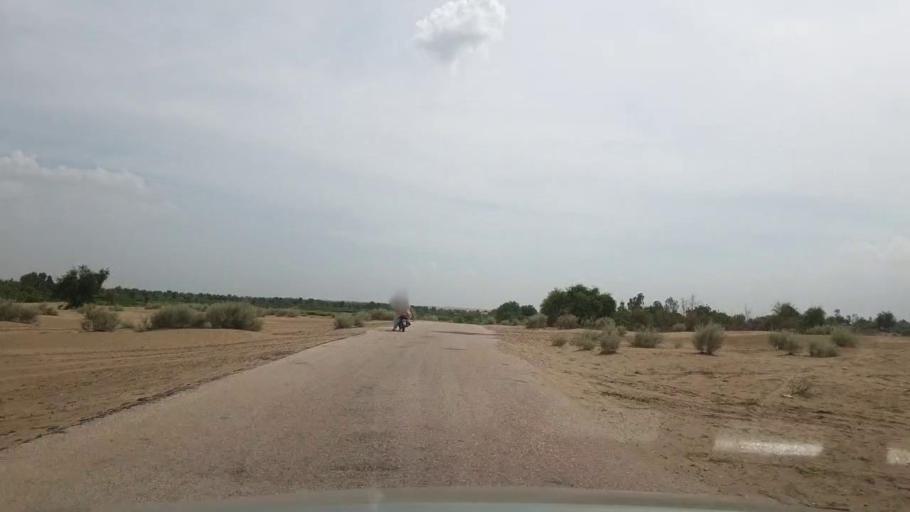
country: PK
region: Sindh
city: Kot Diji
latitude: 27.1501
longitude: 69.0322
